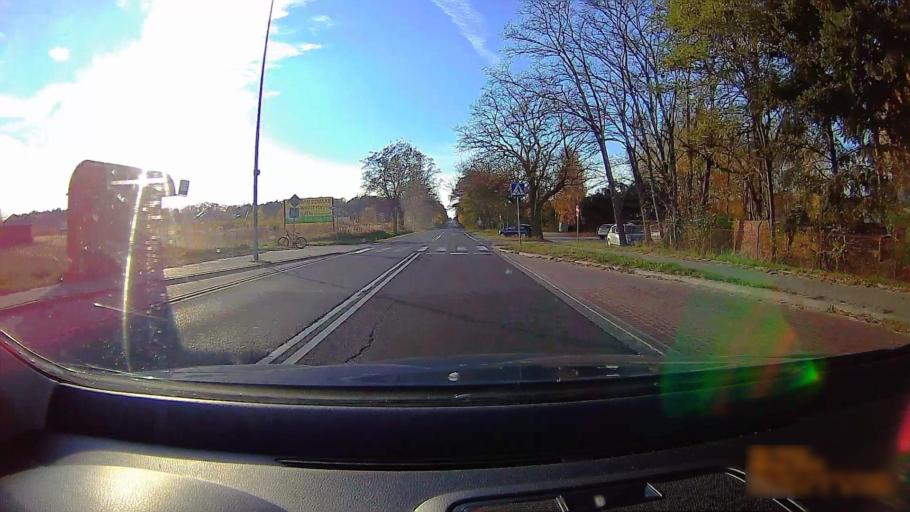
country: PL
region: Greater Poland Voivodeship
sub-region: Powiat koninski
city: Stare Miasto
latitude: 52.2026
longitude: 18.2103
